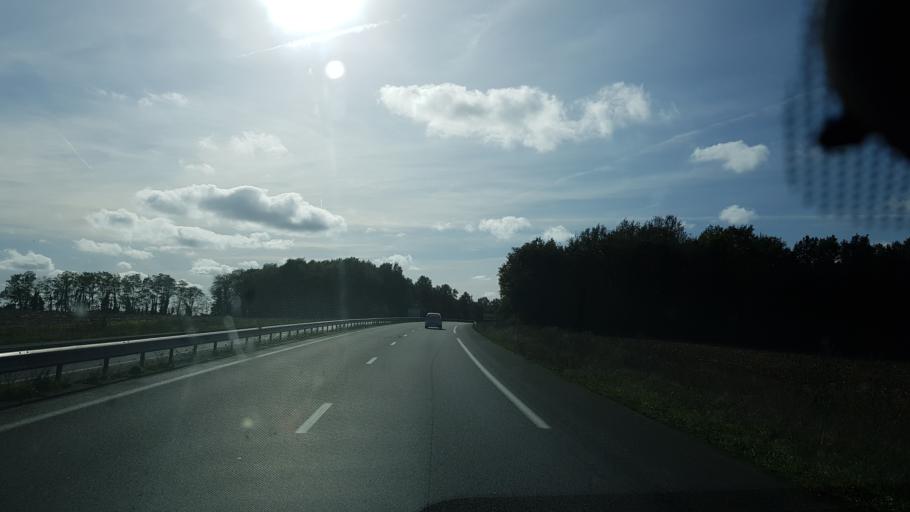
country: FR
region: Poitou-Charentes
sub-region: Departement de la Charente
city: Chasseneuil-sur-Bonnieure
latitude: 45.7957
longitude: 0.4324
